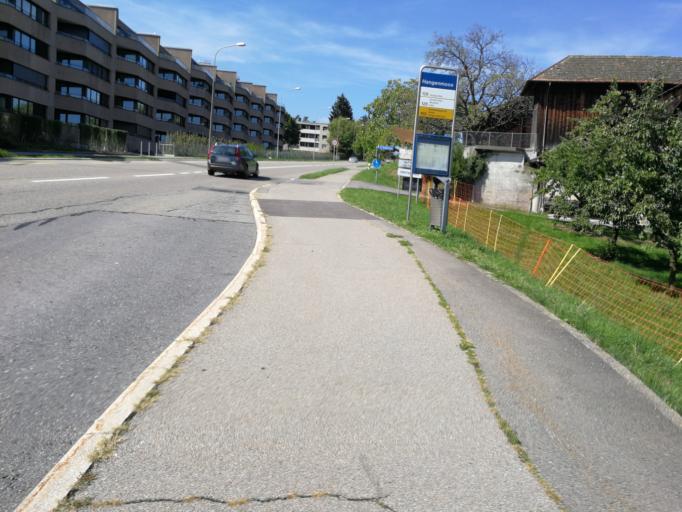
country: CH
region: Zurich
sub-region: Bezirk Horgen
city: Waedenswil / Hangenmoos
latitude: 47.2345
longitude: 8.6532
